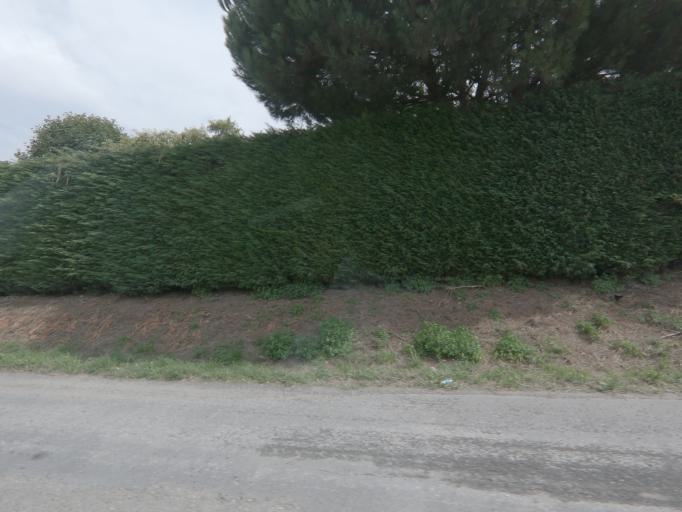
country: PT
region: Leiria
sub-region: Pombal
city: Pombal
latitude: 39.8860
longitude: -8.6709
